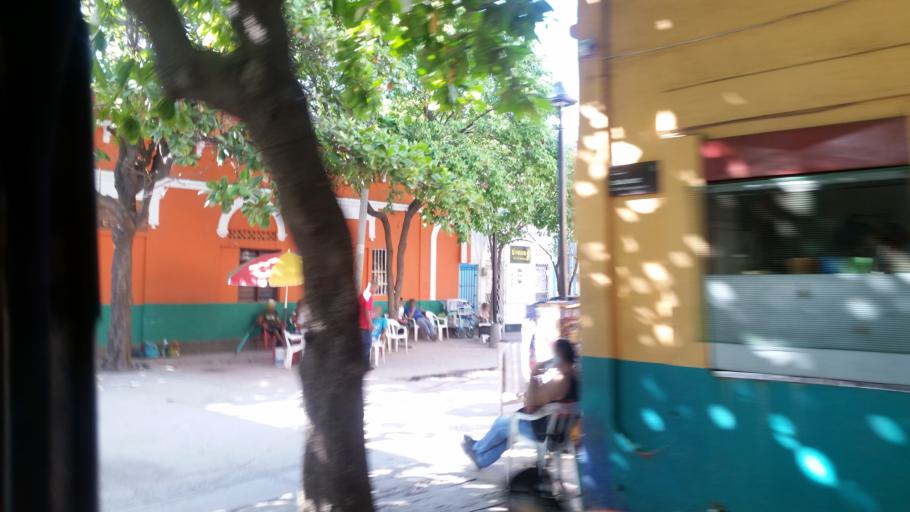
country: CO
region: Magdalena
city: Santa Marta
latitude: 11.2470
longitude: -74.2118
